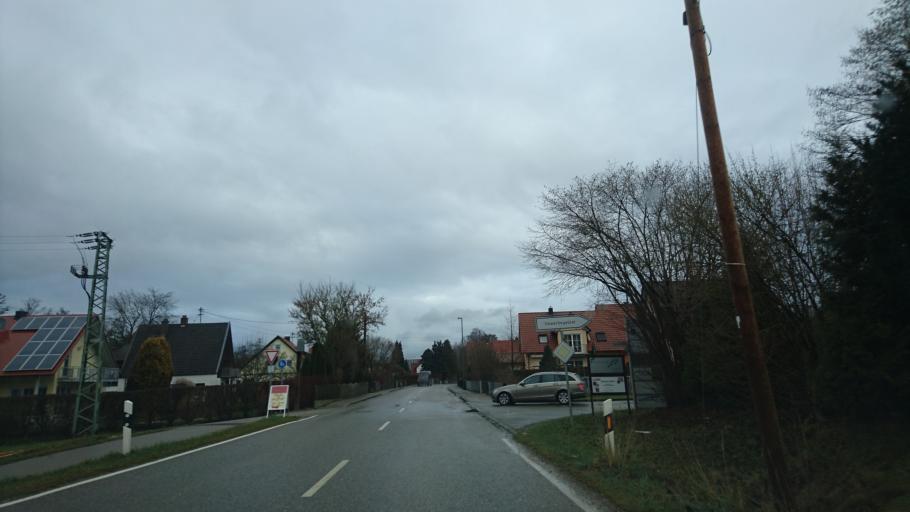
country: DE
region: Bavaria
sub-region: Swabia
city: Biberbach
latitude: 48.5122
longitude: 10.8044
